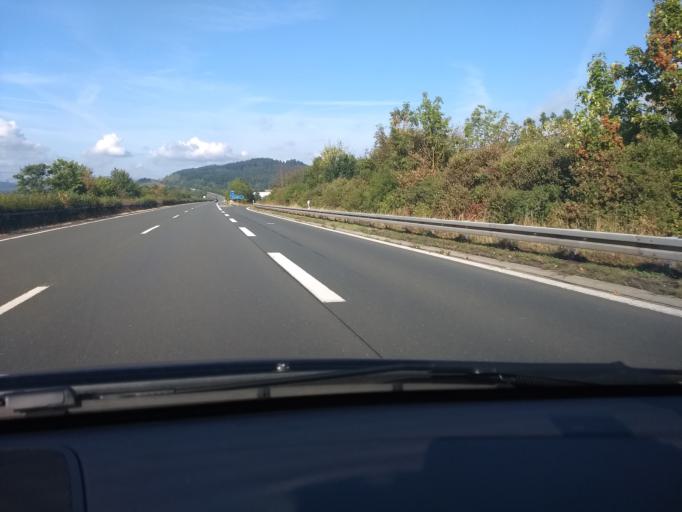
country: DE
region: North Rhine-Westphalia
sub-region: Regierungsbezirk Arnsberg
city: Meschede
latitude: 51.3600
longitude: 8.2538
